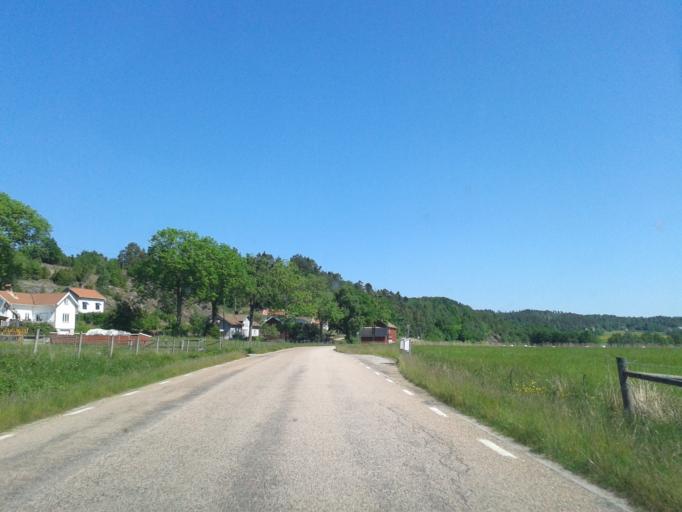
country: SE
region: Vaestra Goetaland
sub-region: Orust
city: Henan
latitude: 58.2519
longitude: 11.7210
